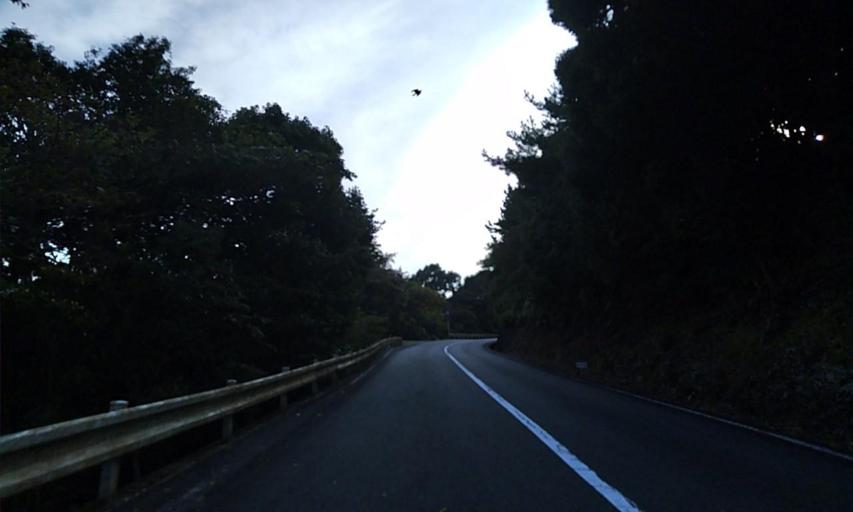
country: JP
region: Mie
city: Toba
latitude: 34.4710
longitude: 136.8285
